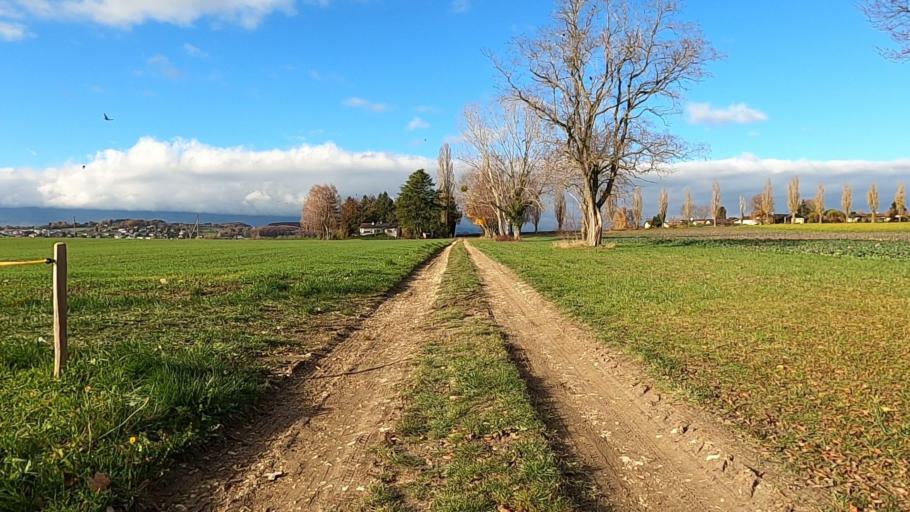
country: CH
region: Vaud
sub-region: Morges District
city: Saint-Prex
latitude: 46.5125
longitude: 6.4483
